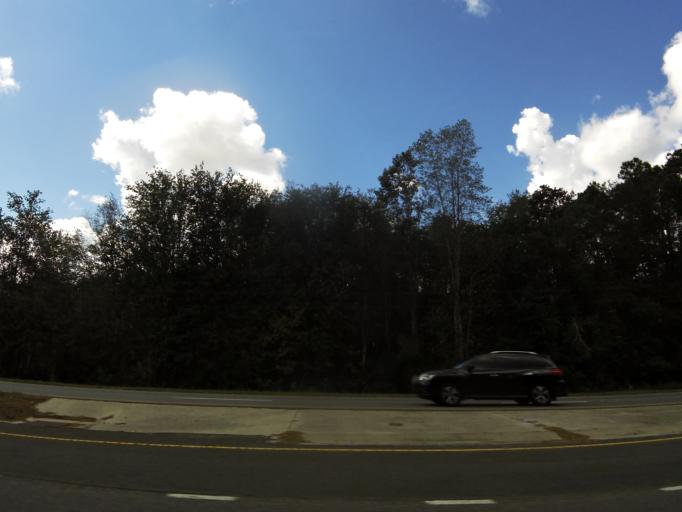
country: US
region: Georgia
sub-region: Charlton County
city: Folkston
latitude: 30.8501
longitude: -82.0088
